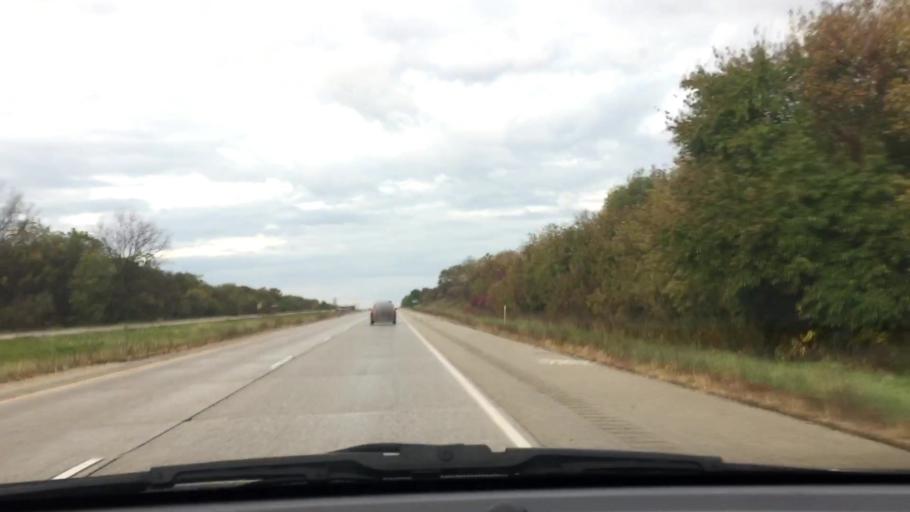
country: US
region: Wisconsin
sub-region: Walworth County
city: Darien
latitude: 42.5817
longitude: -88.7729
